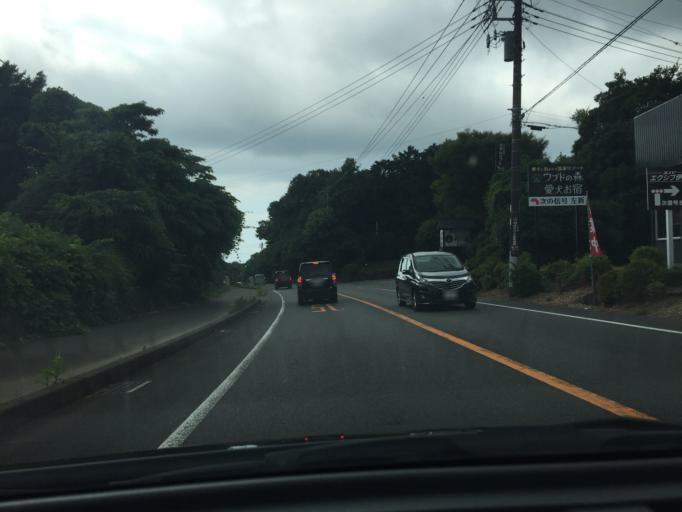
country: JP
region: Shizuoka
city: Ito
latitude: 34.9038
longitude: 139.1200
